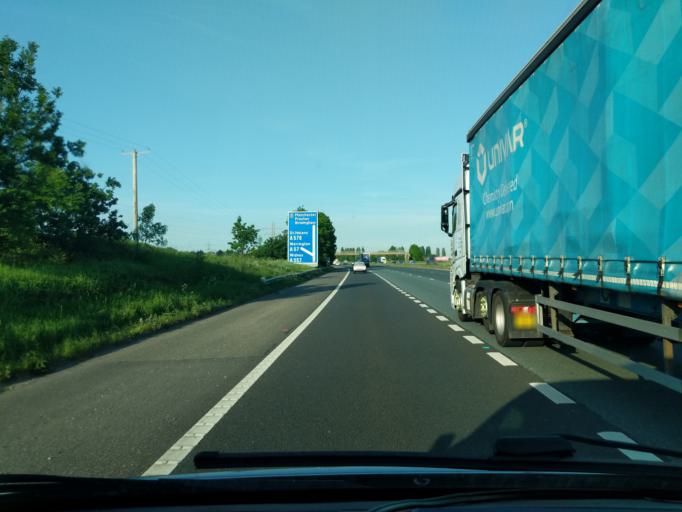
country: GB
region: England
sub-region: Knowsley
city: Whiston
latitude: 53.4006
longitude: -2.7628
